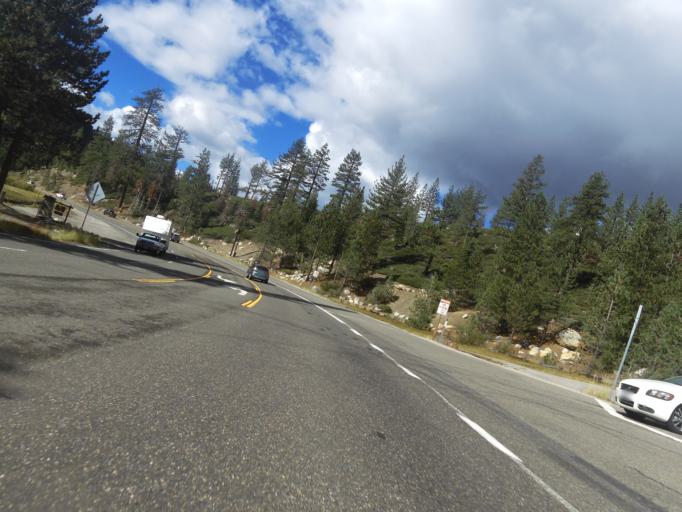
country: US
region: California
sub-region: El Dorado County
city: South Lake Tahoe
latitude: 38.8037
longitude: -120.1173
